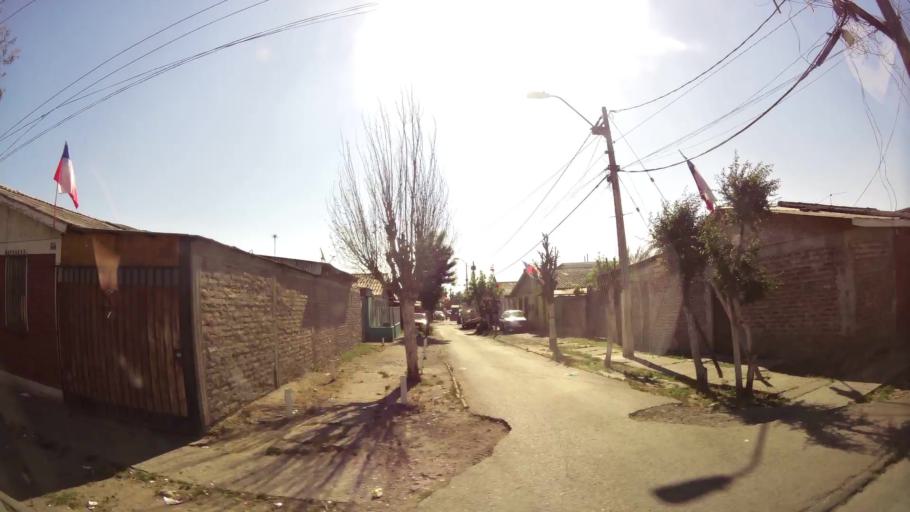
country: CL
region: Santiago Metropolitan
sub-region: Provincia de Maipo
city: San Bernardo
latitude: -33.5171
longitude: -70.6994
